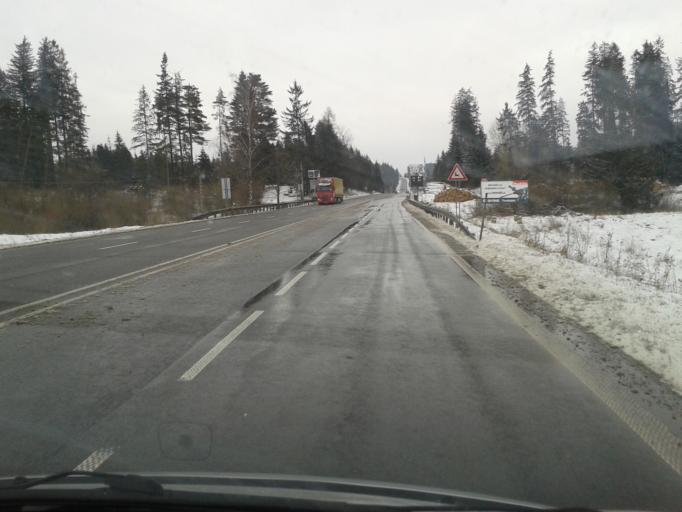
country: PL
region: Lesser Poland Voivodeship
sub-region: Powiat nowotarski
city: Chyzne
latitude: 49.4014
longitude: 19.6518
